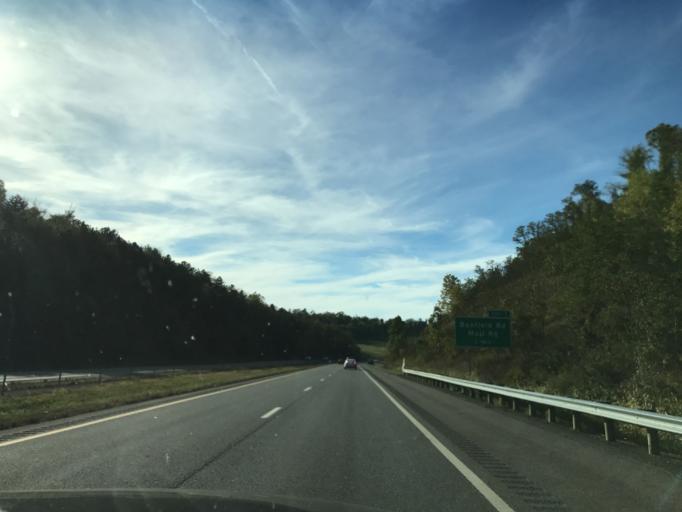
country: US
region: Ohio
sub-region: Belmont County
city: Wolfhurst
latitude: 40.0608
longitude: -80.8343
